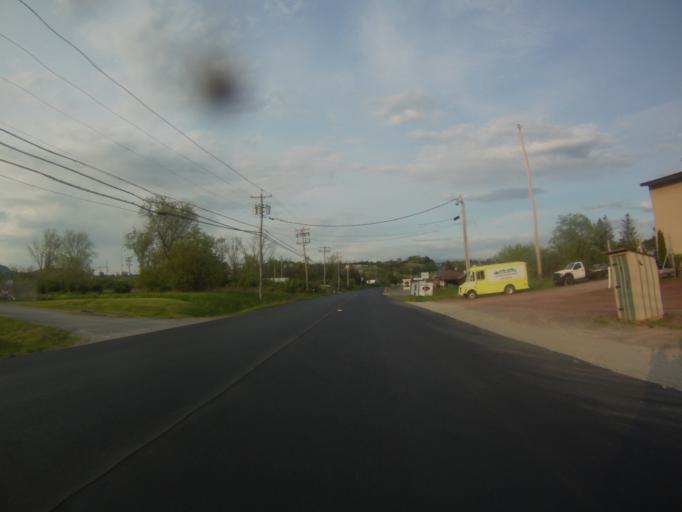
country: US
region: New York
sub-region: Essex County
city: Ticonderoga
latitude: 43.8443
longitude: -73.4473
